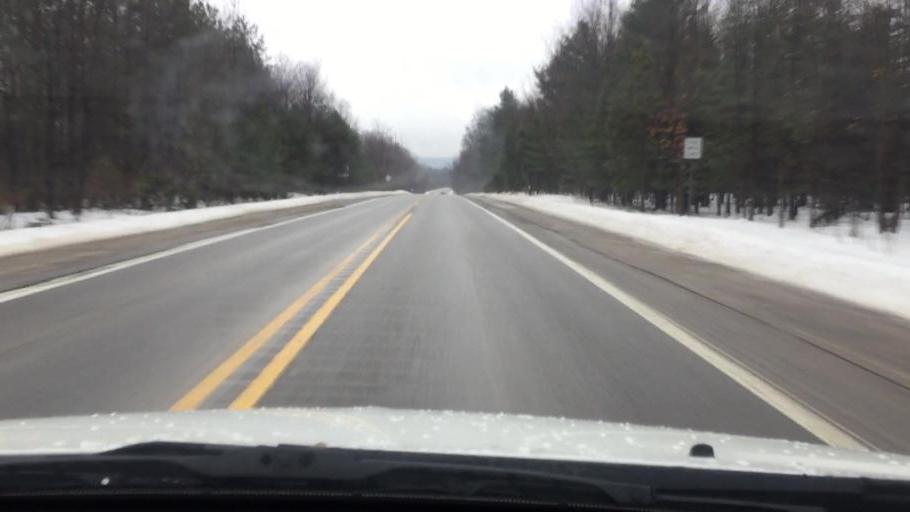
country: US
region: Michigan
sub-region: Charlevoix County
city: Charlevoix
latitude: 45.2653
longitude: -85.2007
